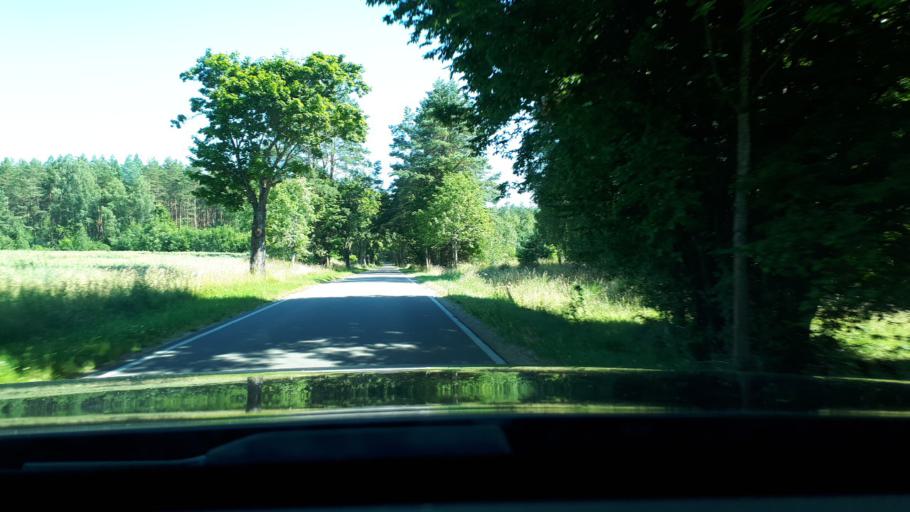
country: PL
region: Warmian-Masurian Voivodeship
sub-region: Powiat olsztynski
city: Stawiguda
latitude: 53.5922
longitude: 20.4319
